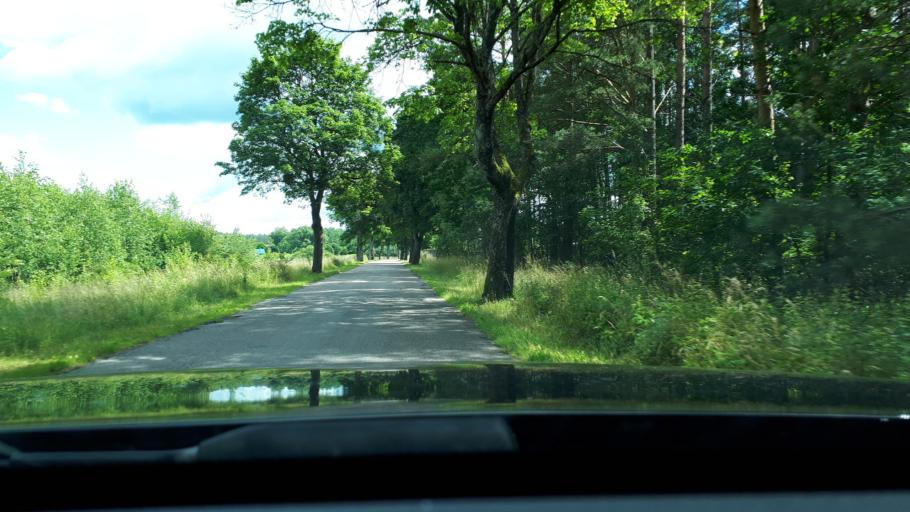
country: PL
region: Warmian-Masurian Voivodeship
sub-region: Powiat olsztynski
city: Olsztynek
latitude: 53.6143
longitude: 20.2424
